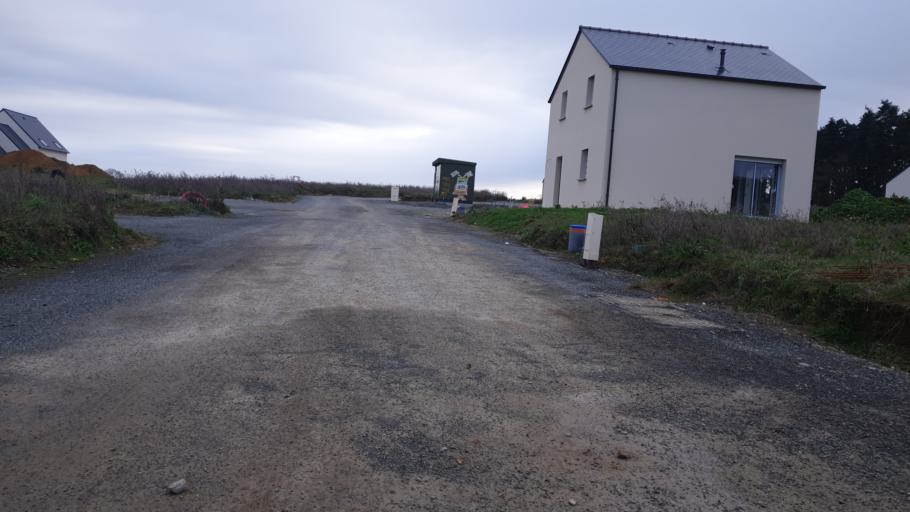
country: FR
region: Brittany
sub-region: Departement d'Ille-et-Vilaine
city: Chanteloup
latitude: 47.9687
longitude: -1.6104
